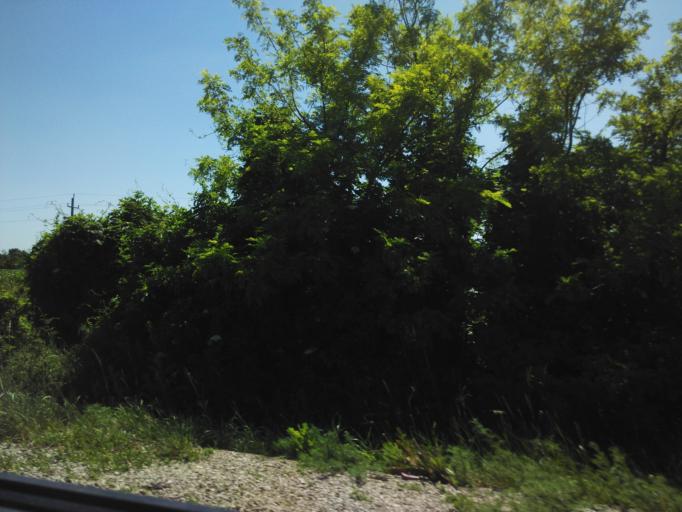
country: HU
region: Fejer
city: Kincsesbanya
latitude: 47.2843
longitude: 18.3109
